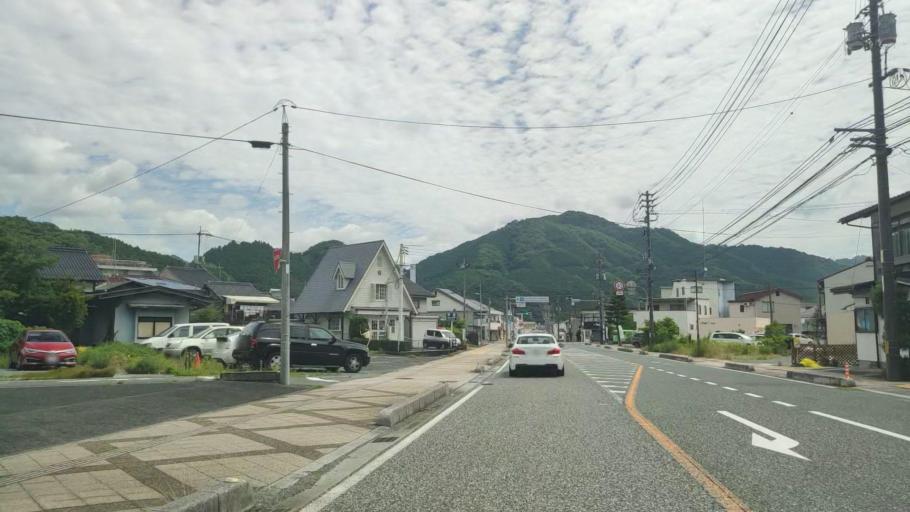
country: JP
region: Okayama
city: Niimi
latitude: 35.0801
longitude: 133.6930
